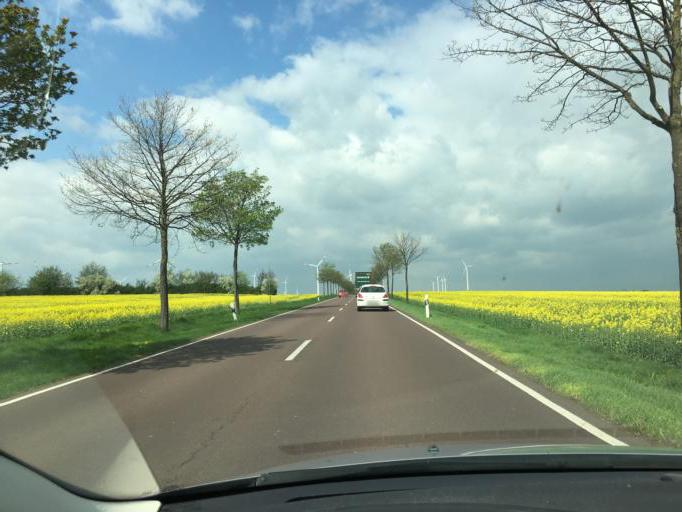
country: DE
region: Saxony-Anhalt
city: Sandersleben
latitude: 51.7206
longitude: 11.5966
